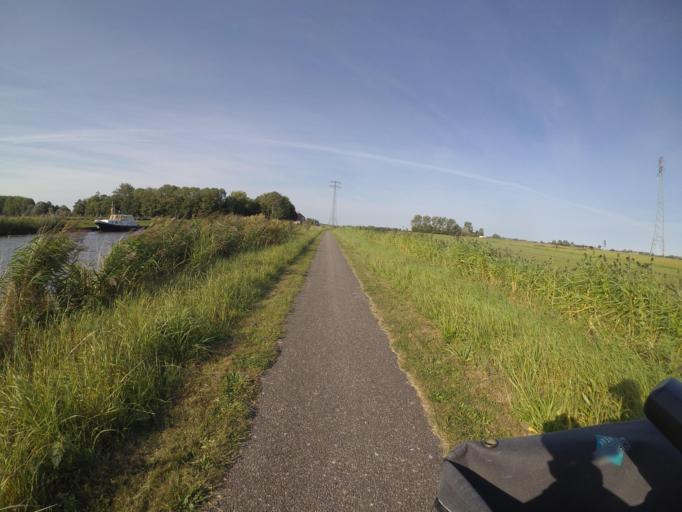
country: NL
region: Friesland
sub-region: Gemeente Dongeradeel
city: Dokkum
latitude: 53.3217
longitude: 5.9783
